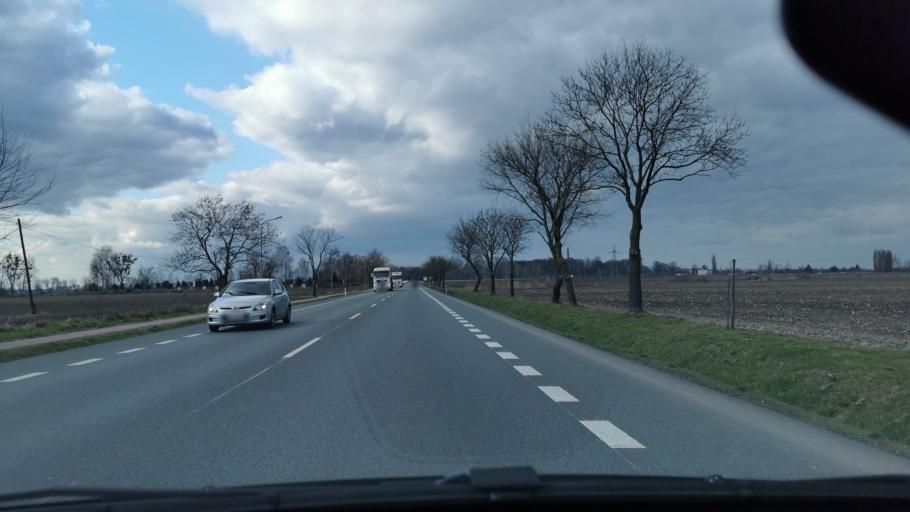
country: PL
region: Masovian Voivodeship
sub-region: Powiat zyrardowski
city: Guzow
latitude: 52.1063
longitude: 20.3442
